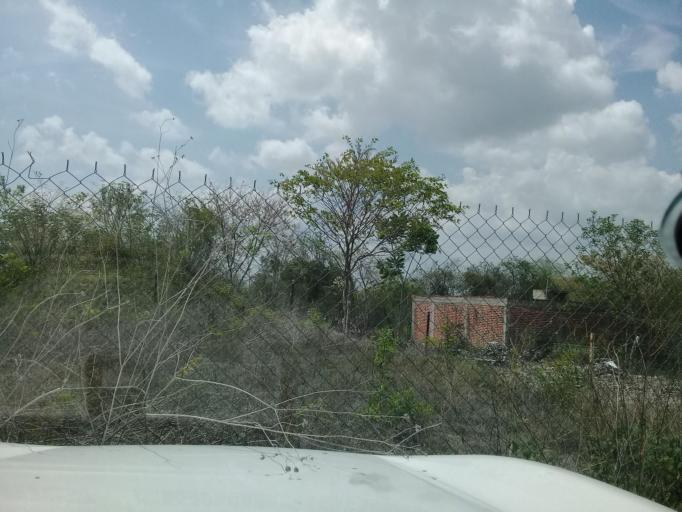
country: MX
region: Veracruz
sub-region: Emiliano Zapata
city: Plan del Rio
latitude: 19.3495
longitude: -96.6474
